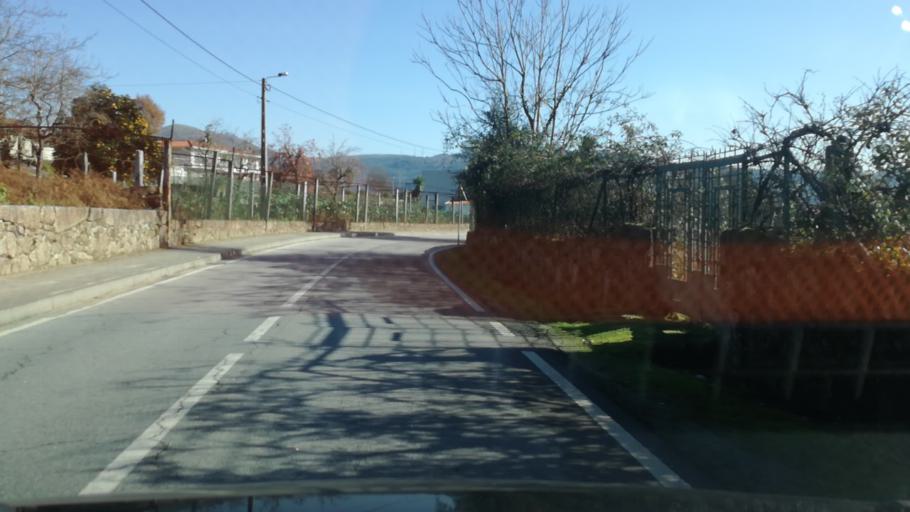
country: PT
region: Braga
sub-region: Guimaraes
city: Ponte
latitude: 41.5162
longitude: -8.3143
